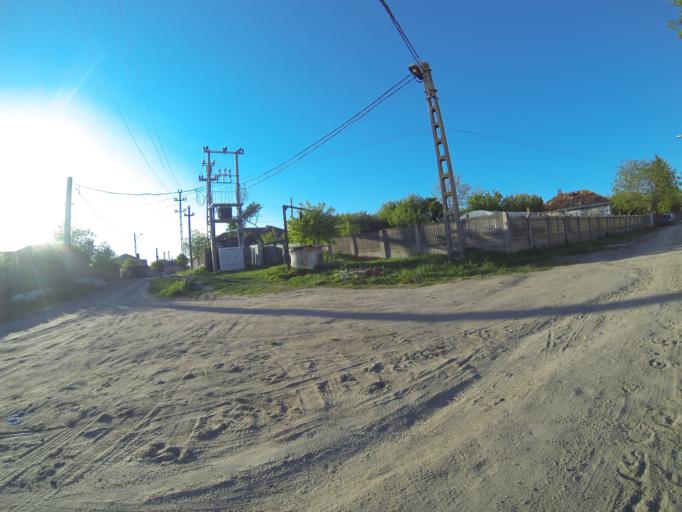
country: RO
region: Dolj
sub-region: Comuna Segarcea
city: Segarcea
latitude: 44.0950
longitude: 23.7379
